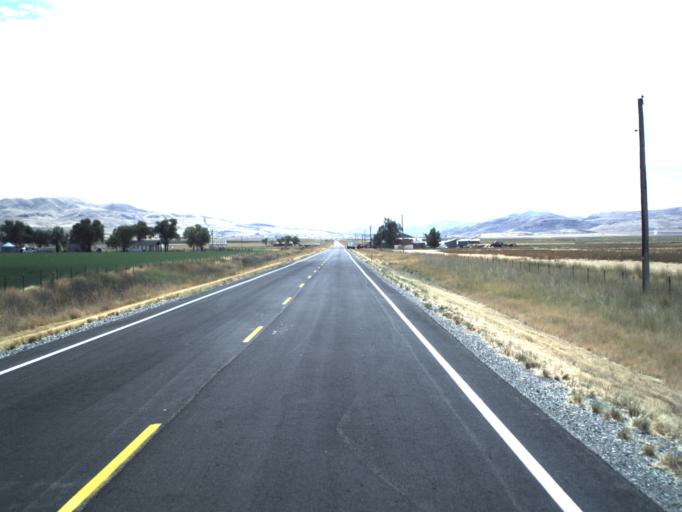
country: US
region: Utah
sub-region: Box Elder County
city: Garland
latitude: 41.7738
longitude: -112.4351
